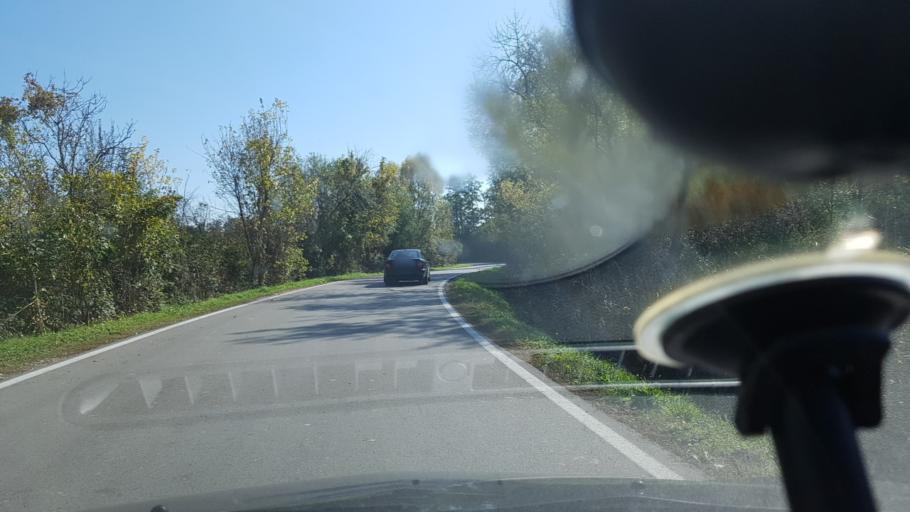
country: HR
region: Zagrebacka
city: Lupoglav
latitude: 45.7345
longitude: 16.2995
